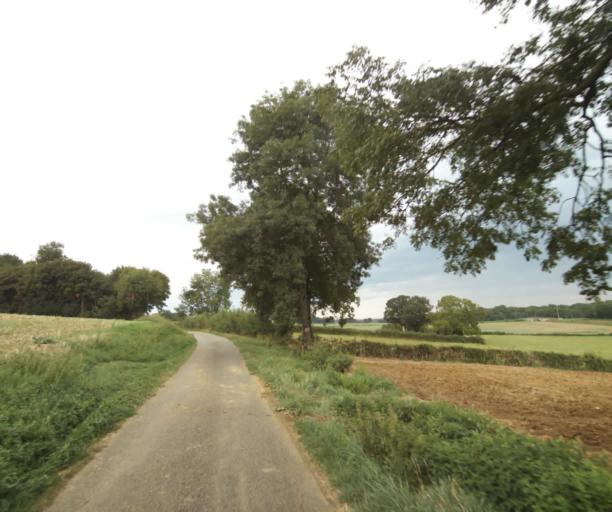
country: FR
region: Bourgogne
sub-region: Departement de Saone-et-Loire
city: Tournus
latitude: 46.5942
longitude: 4.9079
